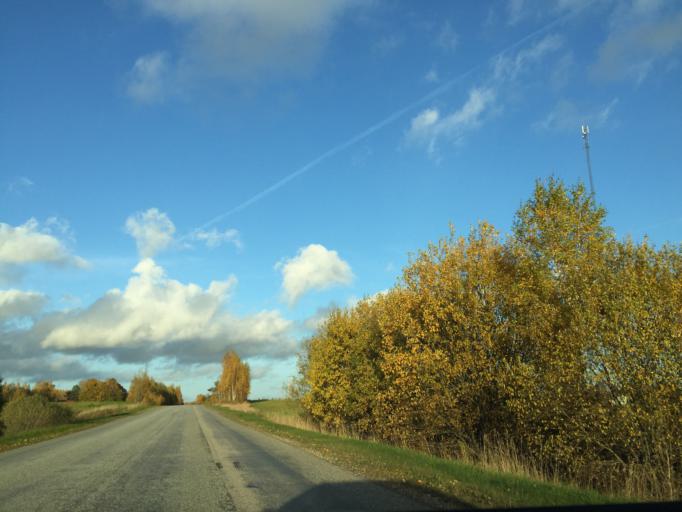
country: LV
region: Ogre
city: Jumprava
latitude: 56.7885
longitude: 25.0297
